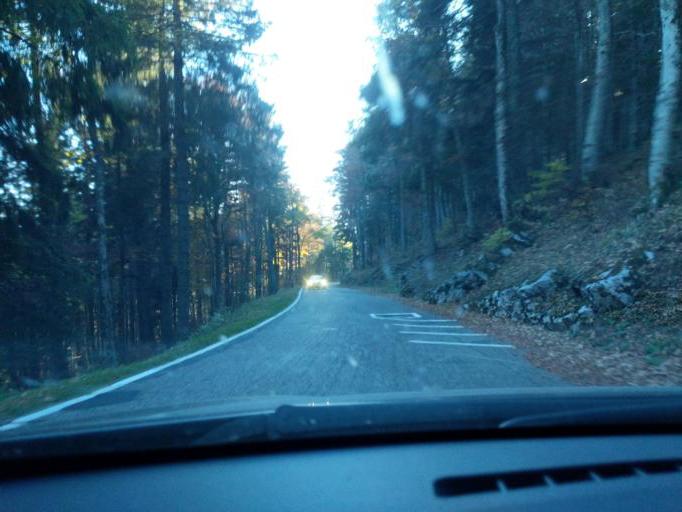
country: CH
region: Bern
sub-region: Jura bernois
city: Saint-Imier
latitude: 47.1153
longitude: 7.0378
